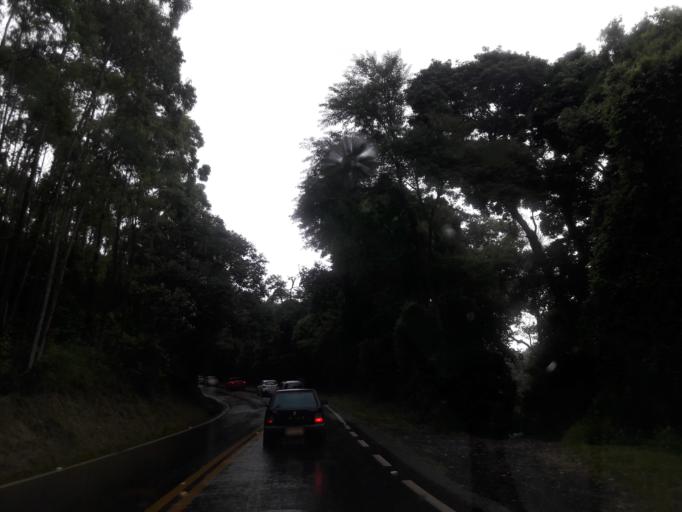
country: BR
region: Sao Paulo
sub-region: Aruja
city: Aruja
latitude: -23.2989
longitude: -46.4261
